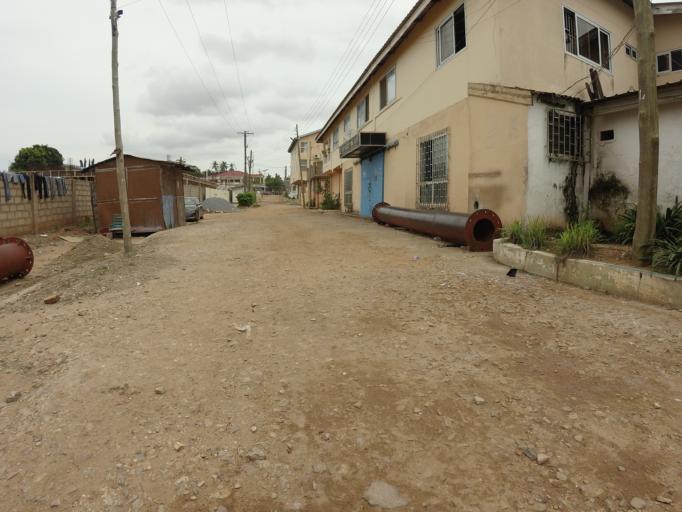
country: GH
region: Greater Accra
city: Dome
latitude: 5.6087
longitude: -0.2252
